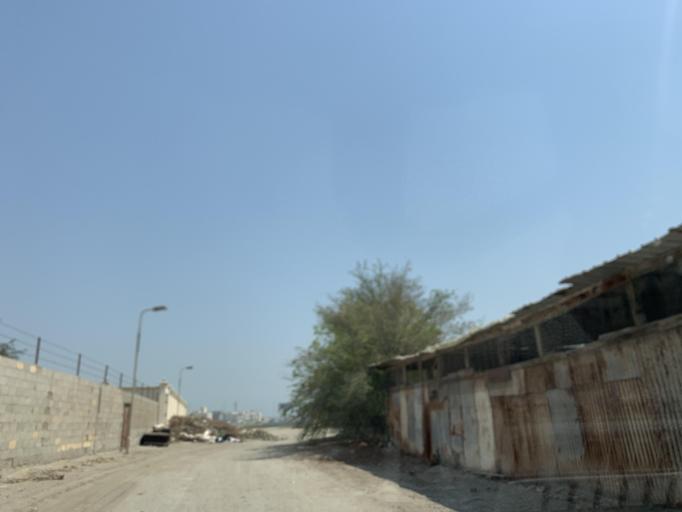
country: BH
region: Manama
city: Jidd Hafs
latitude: 26.2089
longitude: 50.5202
